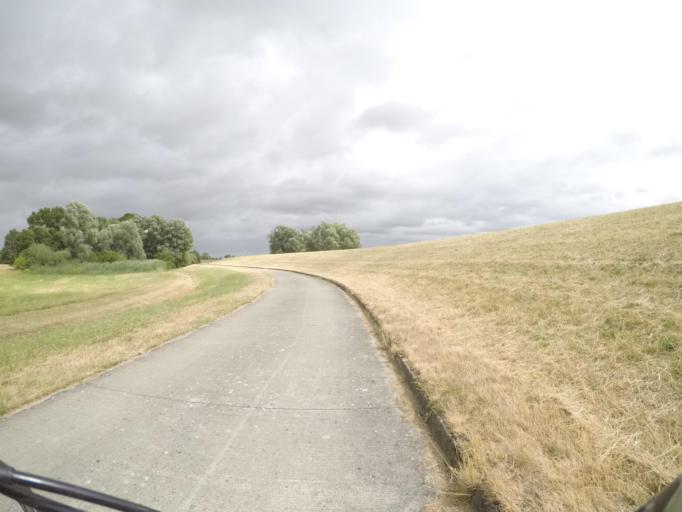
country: DE
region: Lower Saxony
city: Hitzacker
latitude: 53.1487
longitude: 11.0817
